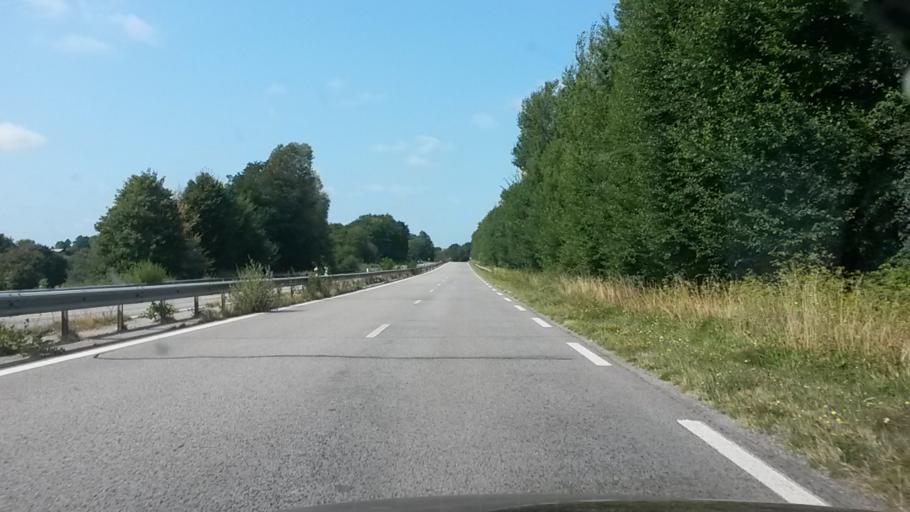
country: FR
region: Lower Normandy
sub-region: Departement de l'Orne
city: Tourouvre
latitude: 48.5757
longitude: 0.6544
